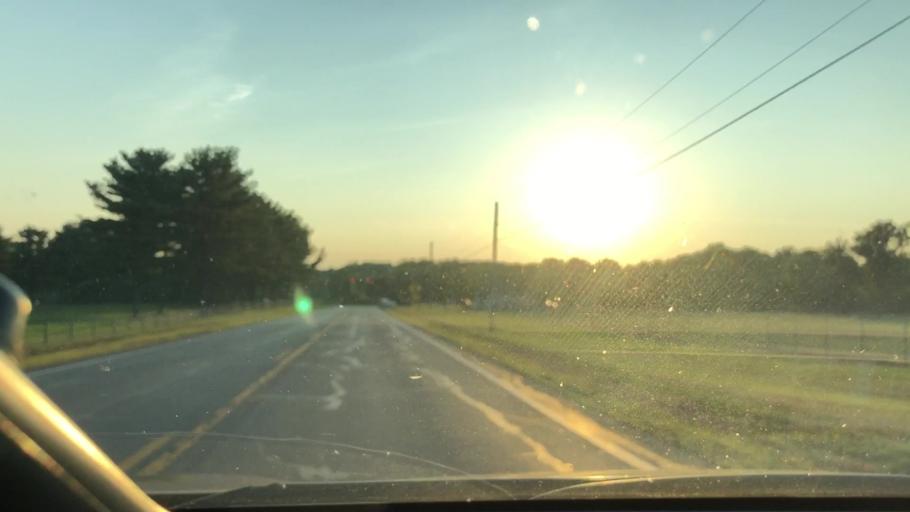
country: US
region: Ohio
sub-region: Summit County
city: Greensburg
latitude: 40.9005
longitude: -81.4650
